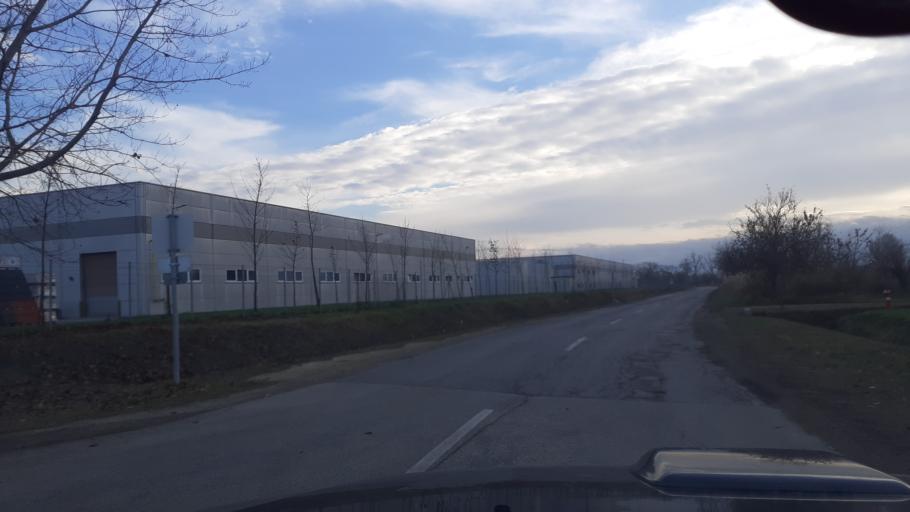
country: HU
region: Bacs-Kiskun
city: Kunszentmiklos
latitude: 47.0114
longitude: 19.1293
